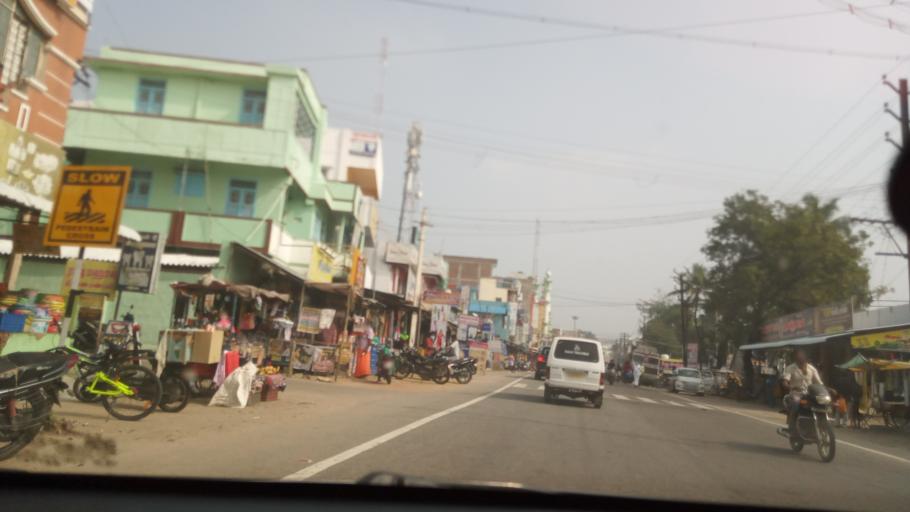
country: IN
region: Tamil Nadu
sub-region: Erode
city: Punjai Puliyampatti
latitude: 11.3495
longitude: 77.1664
